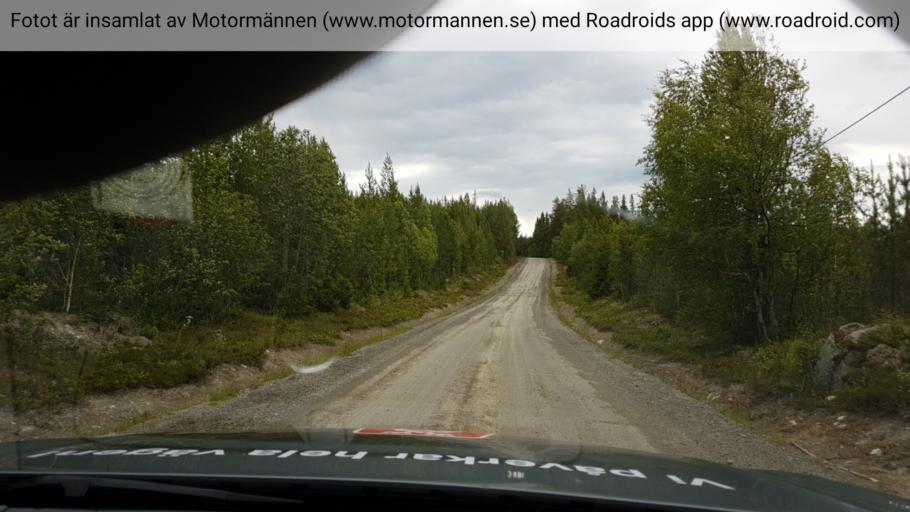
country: SE
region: Jaemtland
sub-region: Bergs Kommun
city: Hoverberg
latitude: 62.7741
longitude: 13.8269
